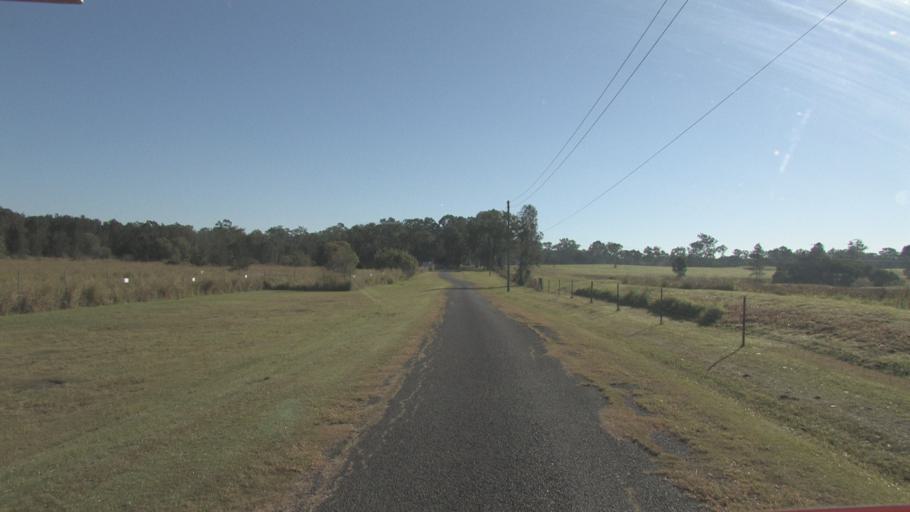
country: AU
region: Queensland
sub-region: Gold Coast
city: Yatala
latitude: -27.6936
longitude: 153.2796
